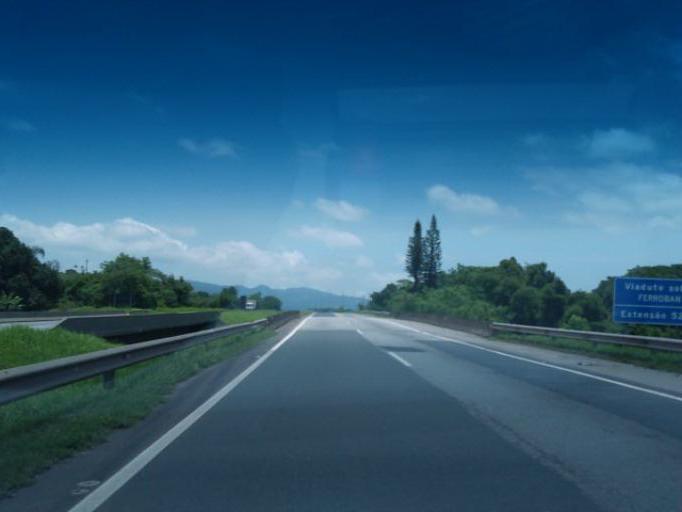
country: BR
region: Sao Paulo
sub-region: Miracatu
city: Miracatu
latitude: -24.2452
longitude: -47.3674
